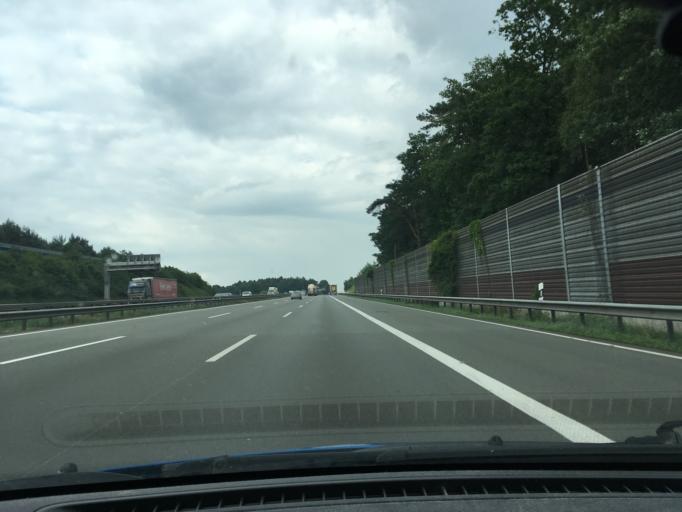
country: DE
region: Lower Saxony
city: Appel
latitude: 53.3666
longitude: 9.7401
